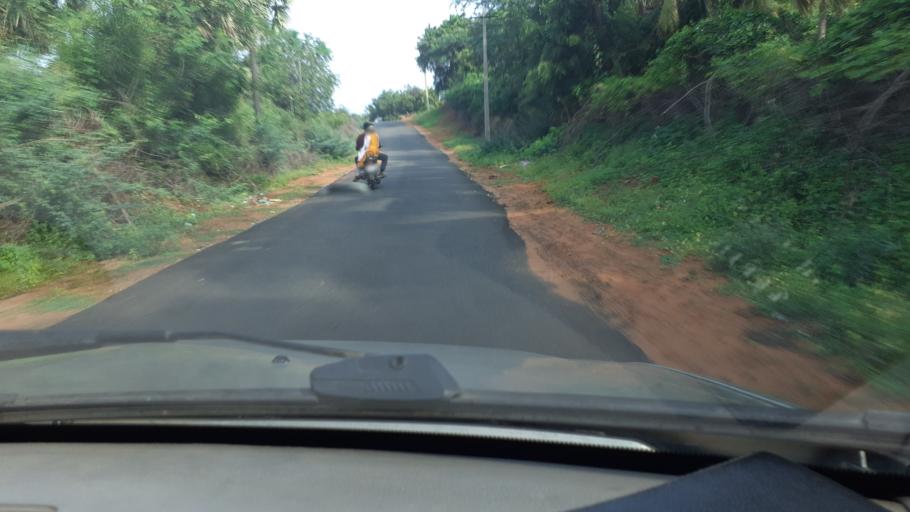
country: IN
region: Tamil Nadu
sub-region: Tirunelveli Kattabo
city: Tisaiyanvilai
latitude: 8.3360
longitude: 77.9510
